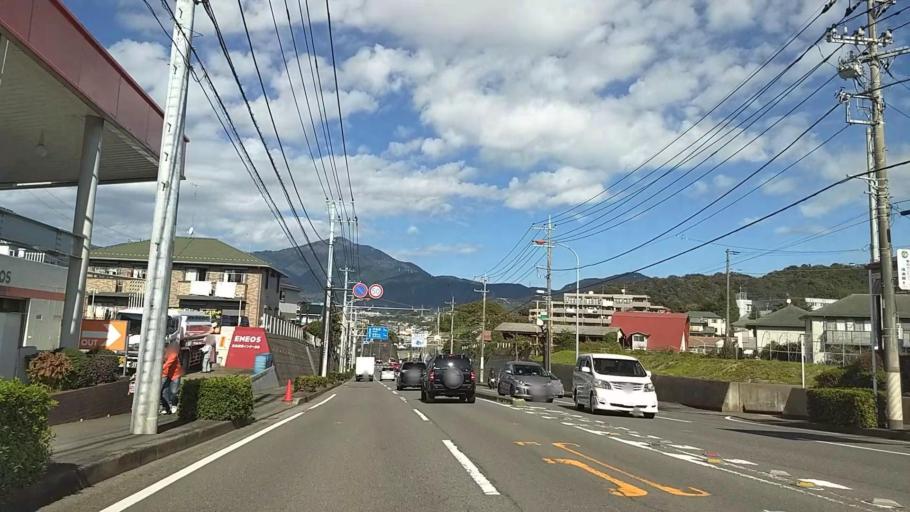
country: JP
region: Kanagawa
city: Hadano
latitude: 35.3619
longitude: 139.2339
